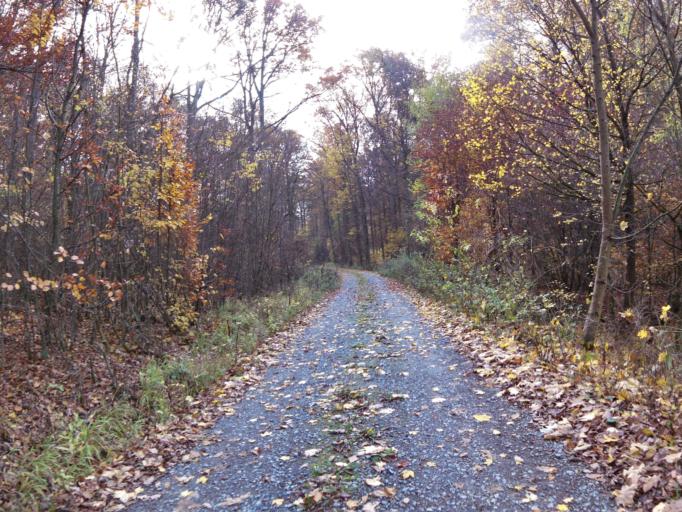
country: DE
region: Bavaria
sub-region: Regierungsbezirk Unterfranken
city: Waldbrunn
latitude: 49.7541
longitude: 9.8121
